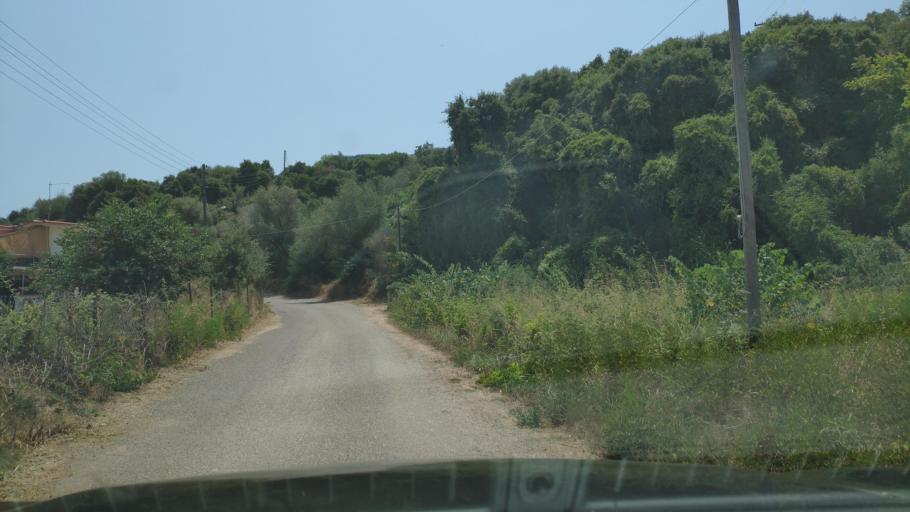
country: GR
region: West Greece
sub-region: Nomos Aitolias kai Akarnanias
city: Amfilochia
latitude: 38.8692
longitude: 21.0725
